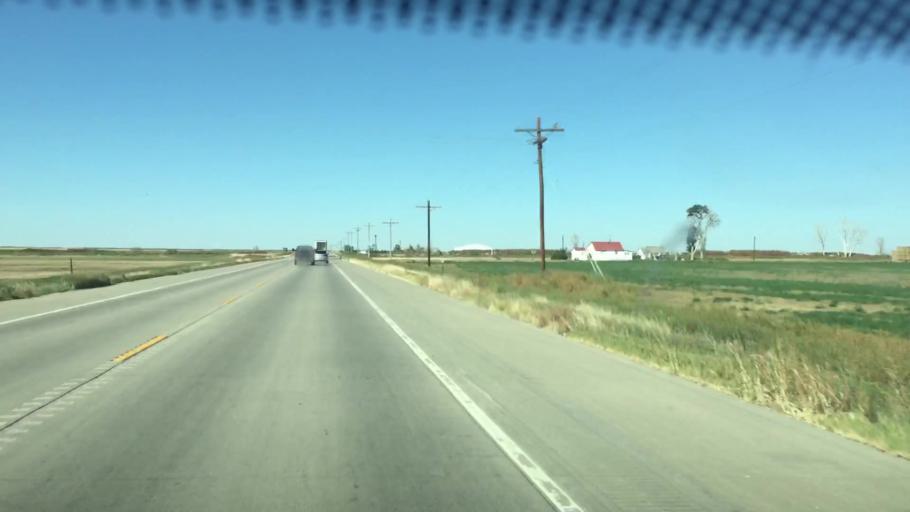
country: US
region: Colorado
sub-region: Prowers County
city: Lamar
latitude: 38.2253
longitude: -102.7240
